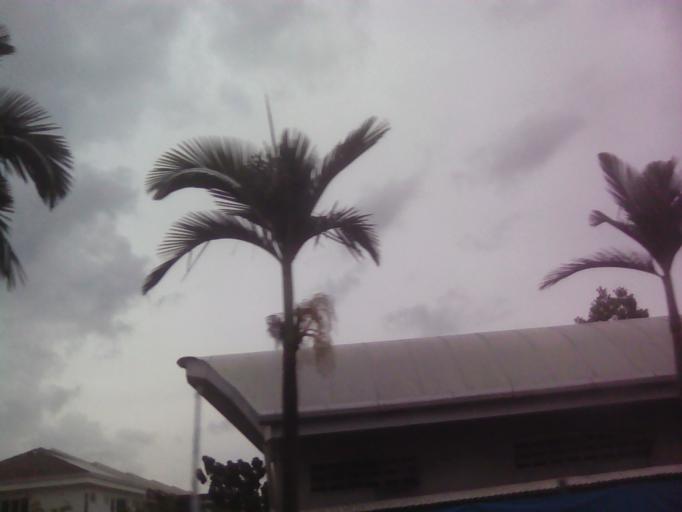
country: MY
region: Penang
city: Butterworth
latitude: 5.4060
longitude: 100.3817
